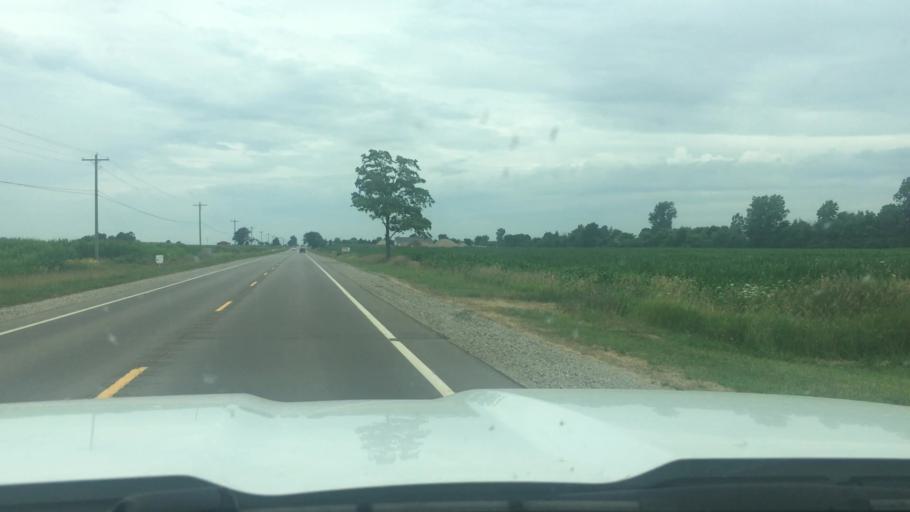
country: US
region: Michigan
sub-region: Clinton County
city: Fowler
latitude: 43.0018
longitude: -84.6881
